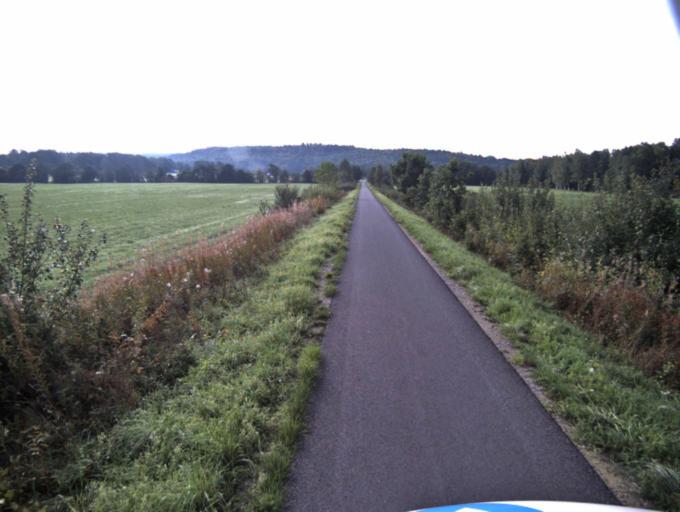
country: SE
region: Vaestra Goetaland
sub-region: Ulricehamns Kommun
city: Ulricehamn
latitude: 57.7383
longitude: 13.4034
